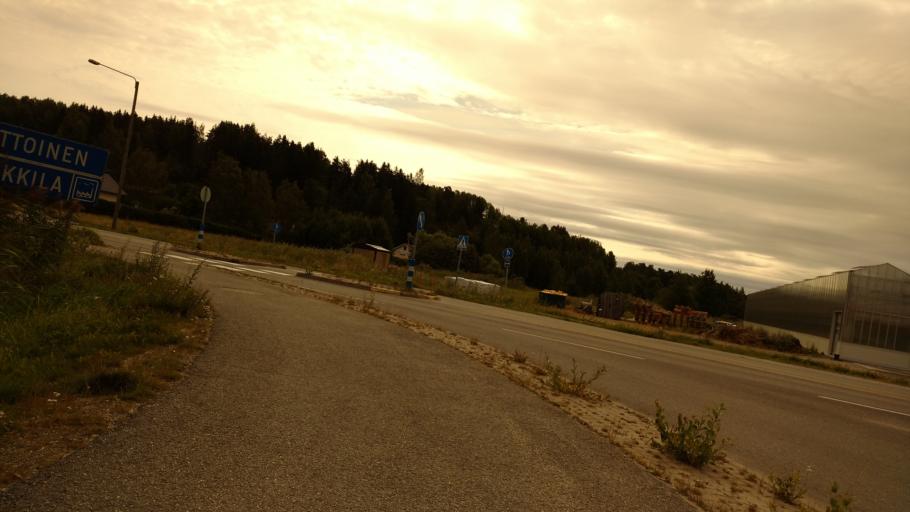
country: FI
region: Varsinais-Suomi
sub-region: Turku
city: Piikkioe
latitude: 60.4260
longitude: 22.4862
